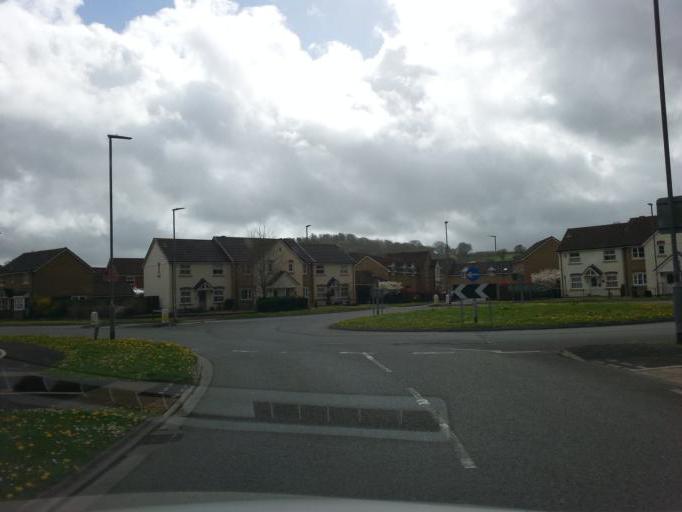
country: GB
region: England
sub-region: Somerset
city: Ilminster
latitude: 50.9290
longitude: -2.9244
